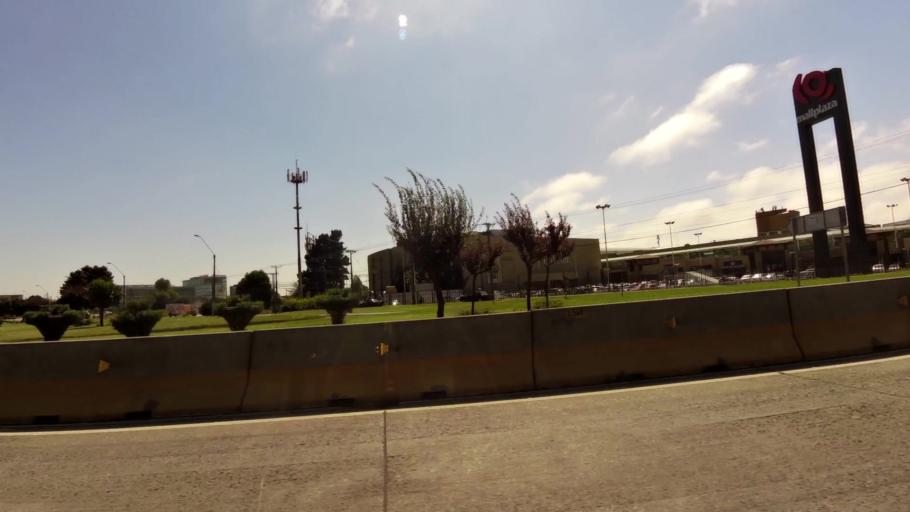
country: CL
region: Biobio
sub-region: Provincia de Concepcion
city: Concepcion
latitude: -36.7938
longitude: -73.0648
